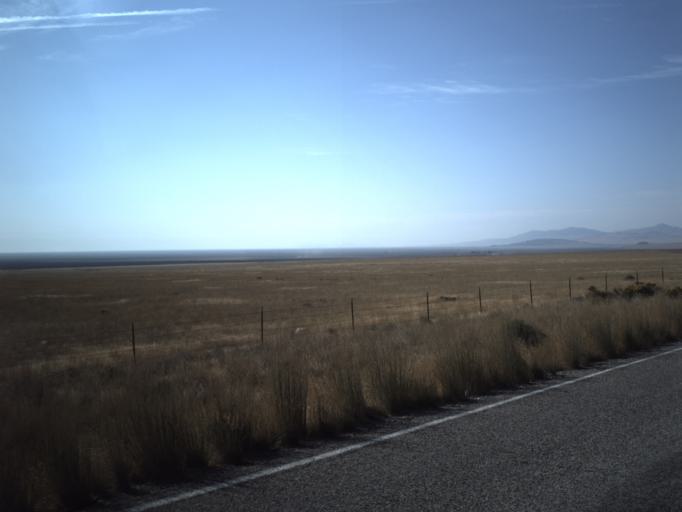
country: US
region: Idaho
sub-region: Minidoka County
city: Rupert
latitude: 41.8513
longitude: -113.1339
